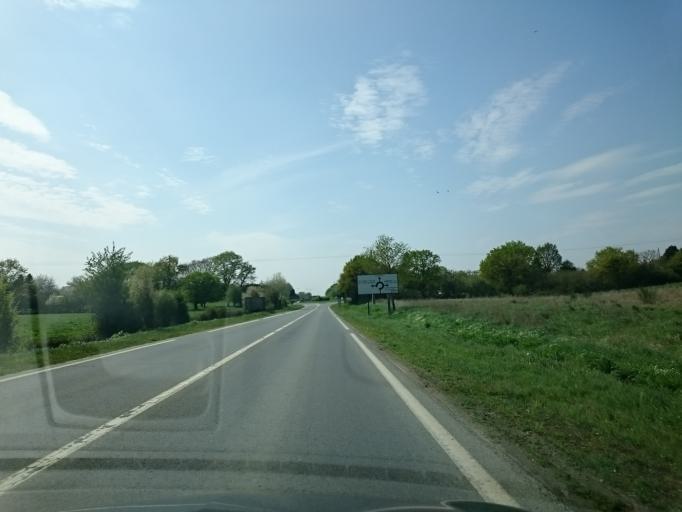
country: FR
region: Brittany
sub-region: Departement d'Ille-et-Vilaine
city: Chantepie
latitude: 48.0795
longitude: -1.6007
